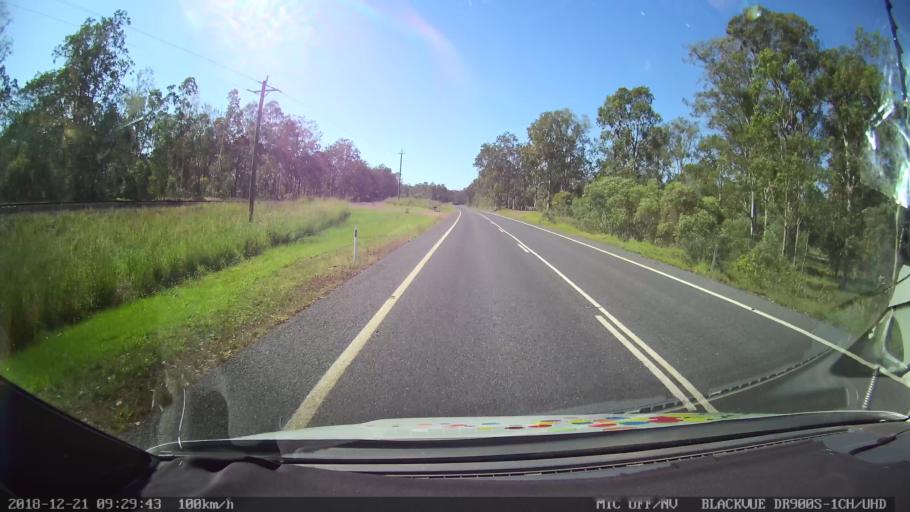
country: AU
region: New South Wales
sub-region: Clarence Valley
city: Maclean
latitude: -29.4360
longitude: 152.9901
